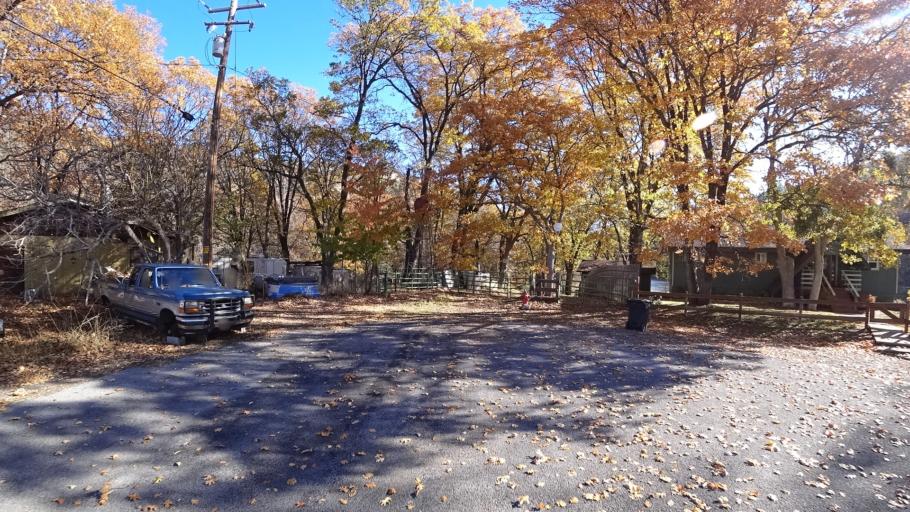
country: US
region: California
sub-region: Siskiyou County
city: Montague
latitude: 41.9659
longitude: -122.2590
